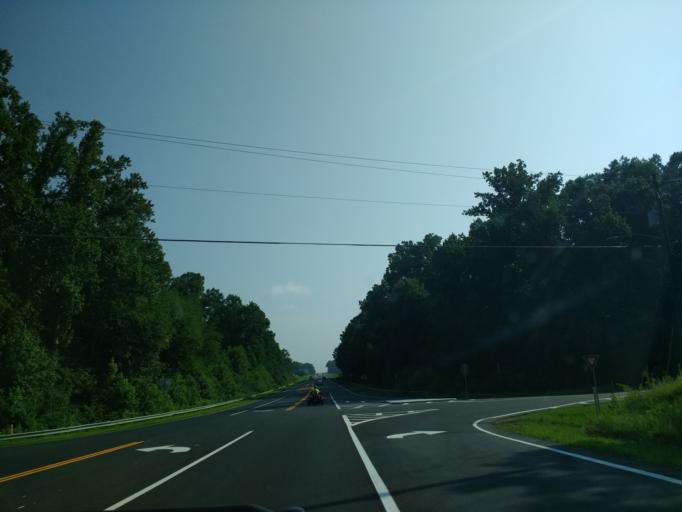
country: US
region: Georgia
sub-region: White County
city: Cleveland
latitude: 34.4773
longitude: -83.7672
